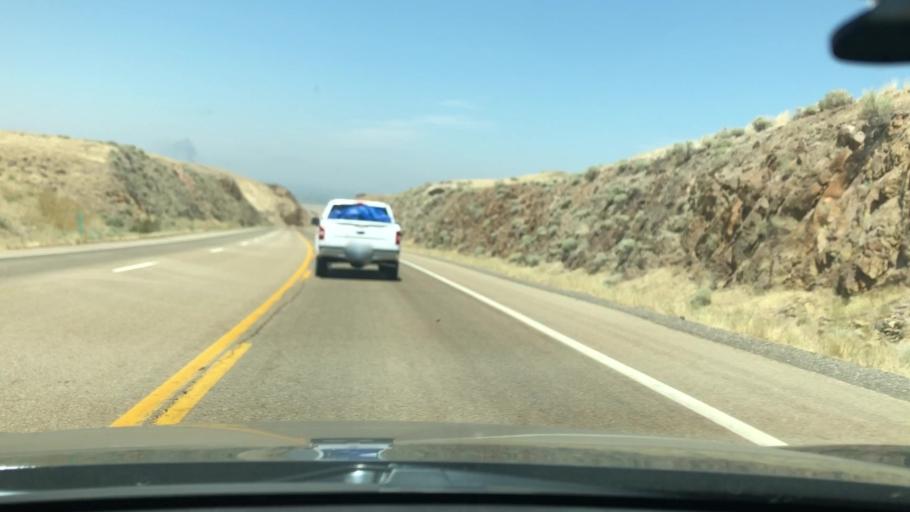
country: US
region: Idaho
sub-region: Owyhee County
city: Marsing
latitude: 43.4272
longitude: -116.8584
